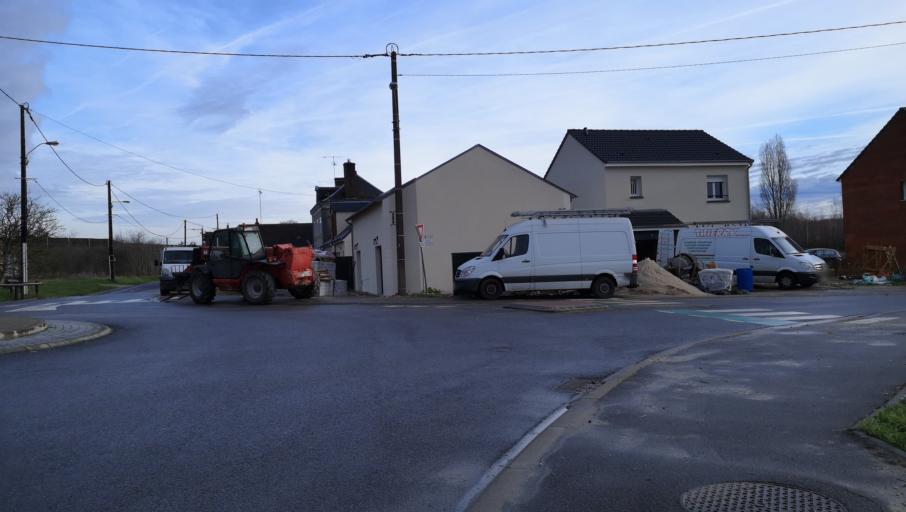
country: FR
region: Centre
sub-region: Departement du Loiret
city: Saint-Jean-de-Braye
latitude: 47.9237
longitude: 1.9709
